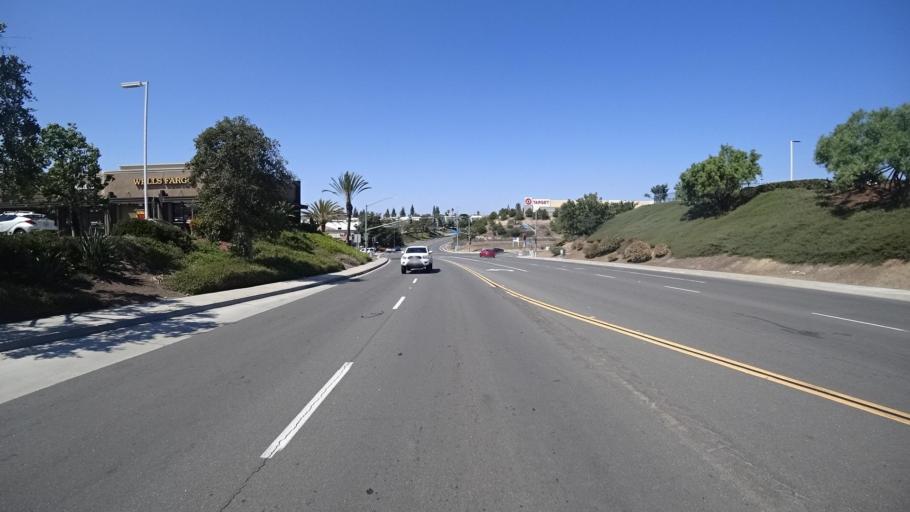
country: US
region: California
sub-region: San Diego County
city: Lake San Marcos
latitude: 33.1338
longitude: -117.2287
